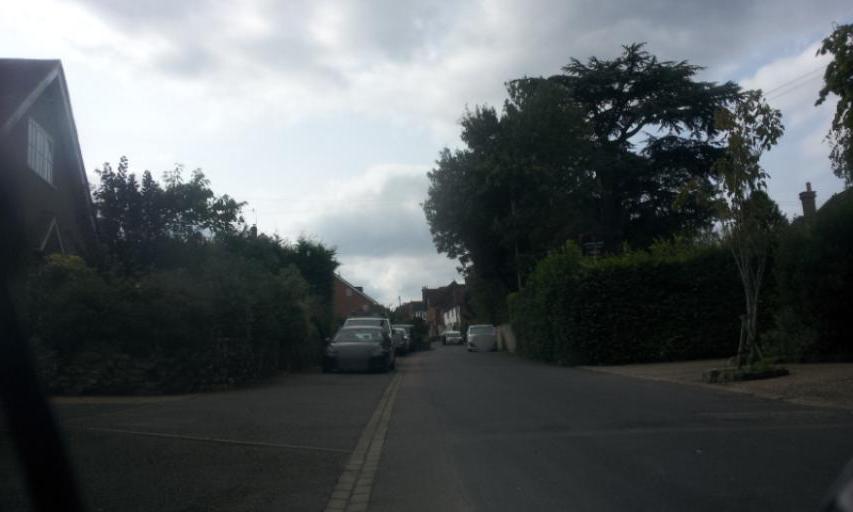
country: GB
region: England
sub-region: Kent
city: Borough Green
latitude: 51.2579
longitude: 0.2983
